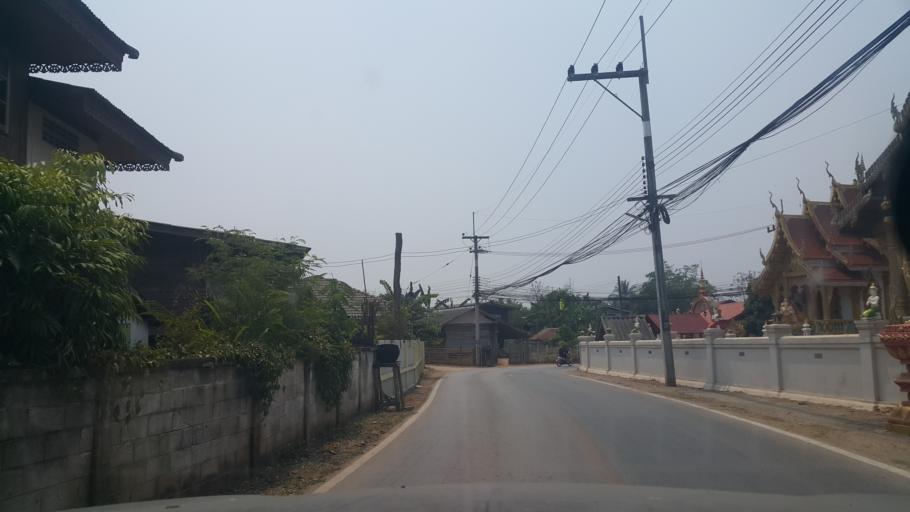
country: TH
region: Lampang
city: Soem Ngam
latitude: 18.0723
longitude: 99.2294
